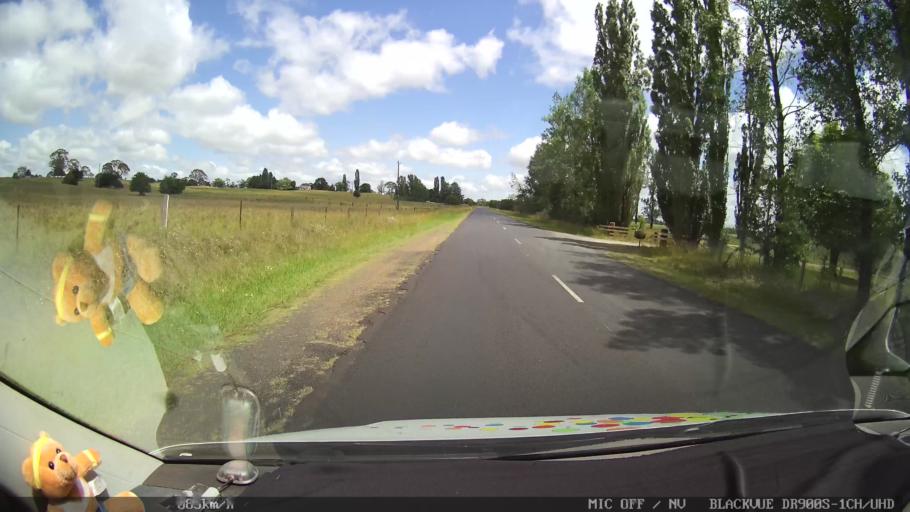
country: AU
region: New South Wales
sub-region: Glen Innes Severn
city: Glen Innes
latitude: -29.7065
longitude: 151.7207
